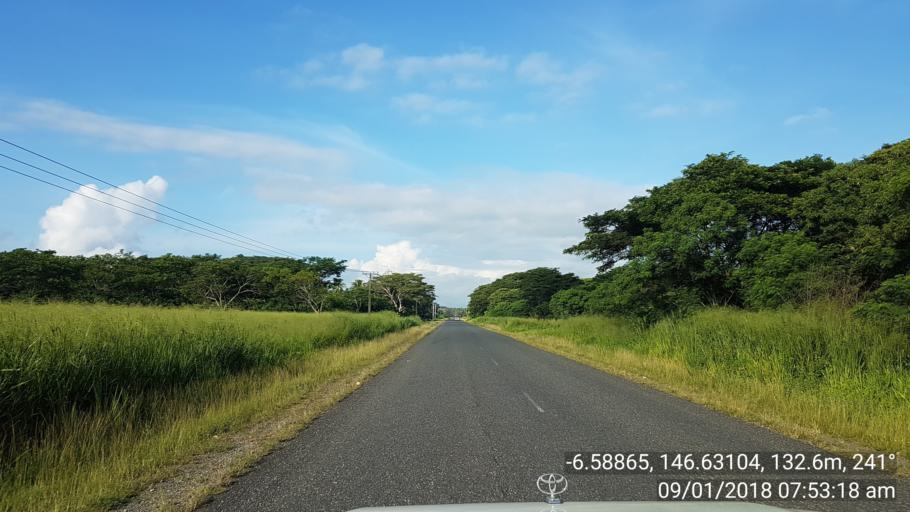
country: PG
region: Morobe
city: Lae
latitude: -6.5884
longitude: 146.6314
